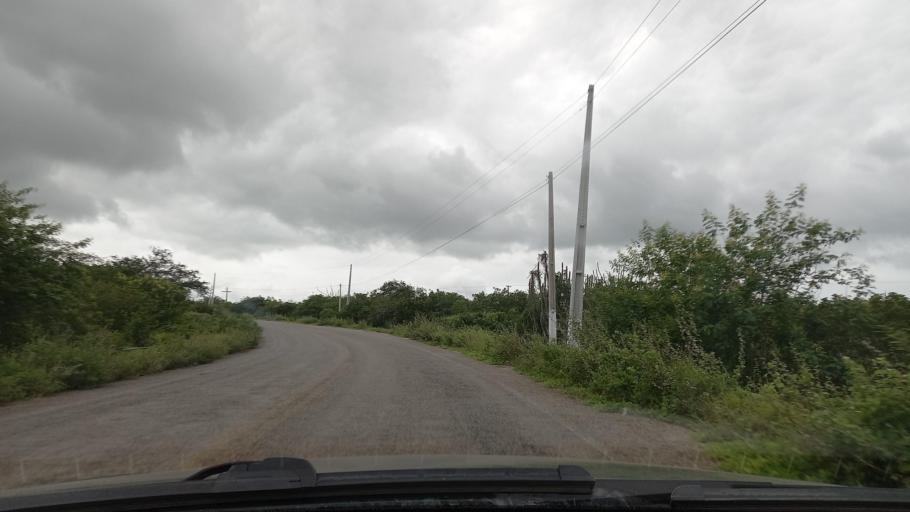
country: BR
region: Sergipe
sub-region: Caninde De Sao Francisco
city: Caninde de Sao Francisco
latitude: -9.6274
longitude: -37.7813
